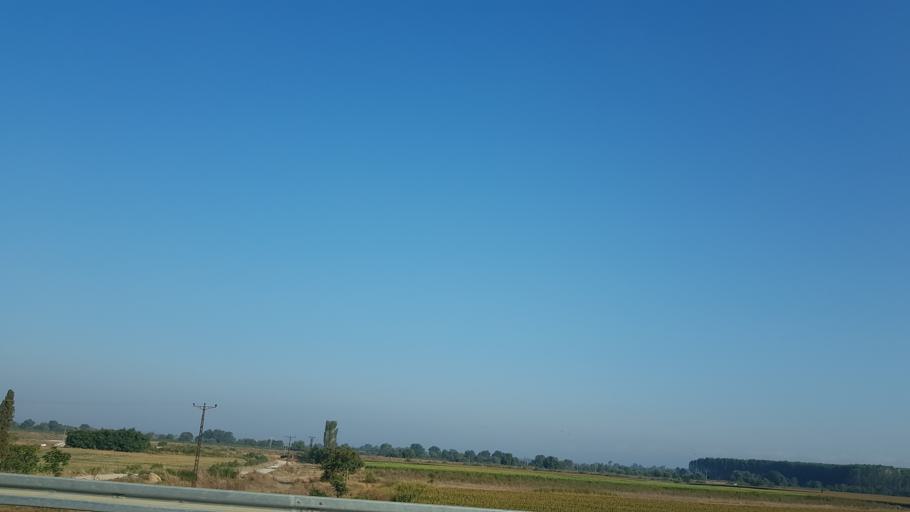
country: TR
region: Bursa
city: Karacabey
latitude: 40.1371
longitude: 28.2979
